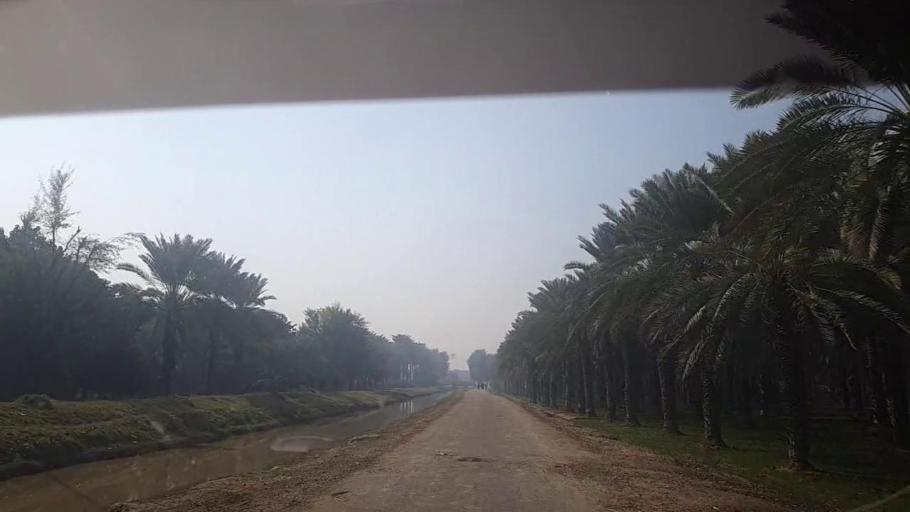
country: PK
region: Sindh
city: Khairpur
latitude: 27.4636
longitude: 68.7096
